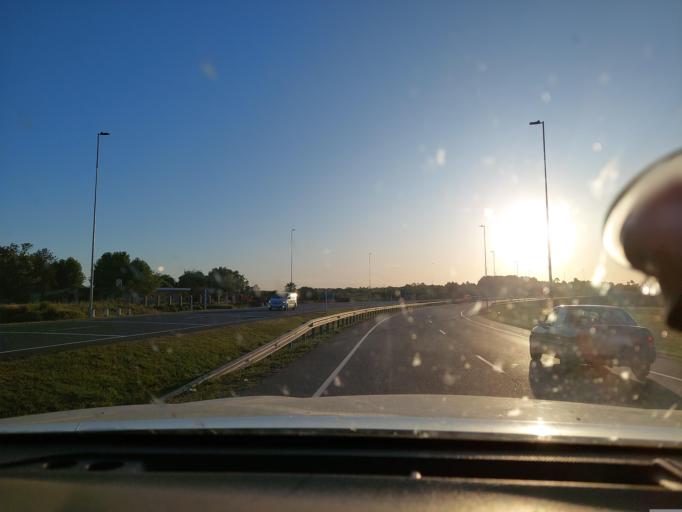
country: UY
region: Canelones
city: Pando
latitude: -34.7117
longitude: -55.9354
